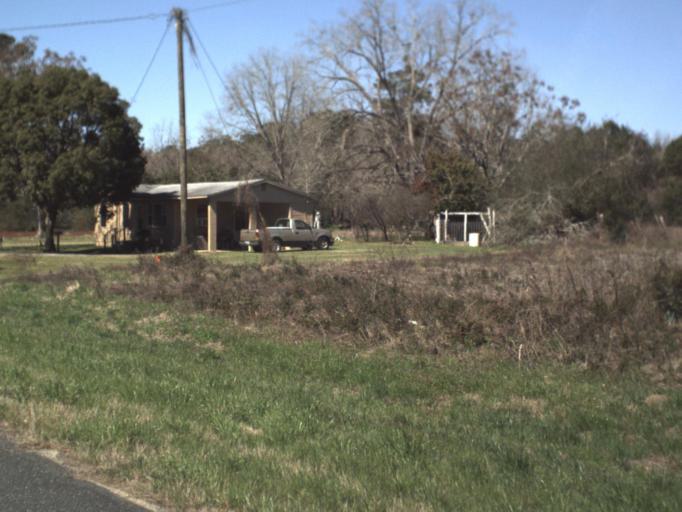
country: US
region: Florida
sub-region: Jackson County
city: Marianna
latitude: 30.7847
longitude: -85.3140
